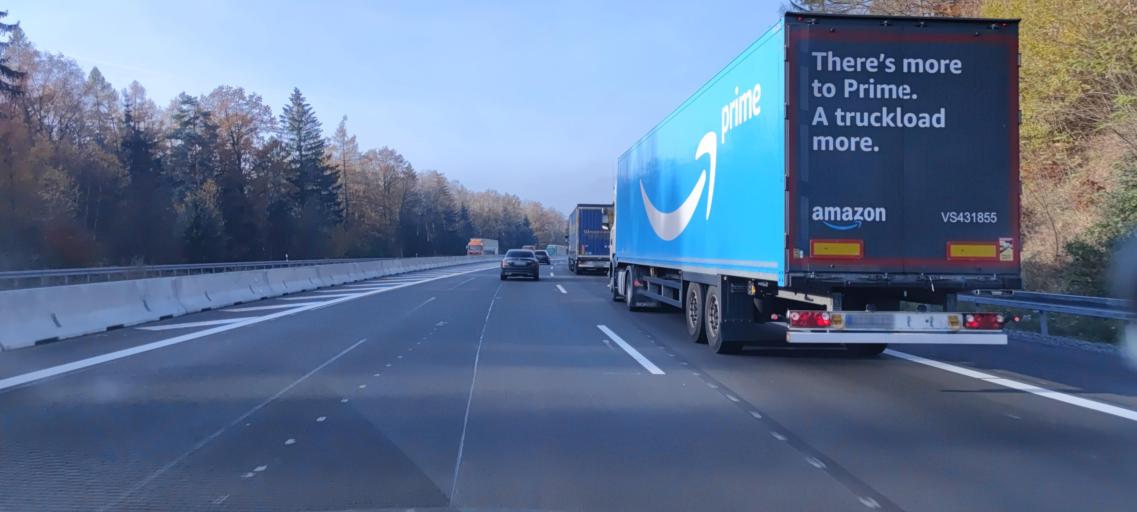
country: DE
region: Saxony
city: Rammenau
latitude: 51.1743
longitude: 14.1246
